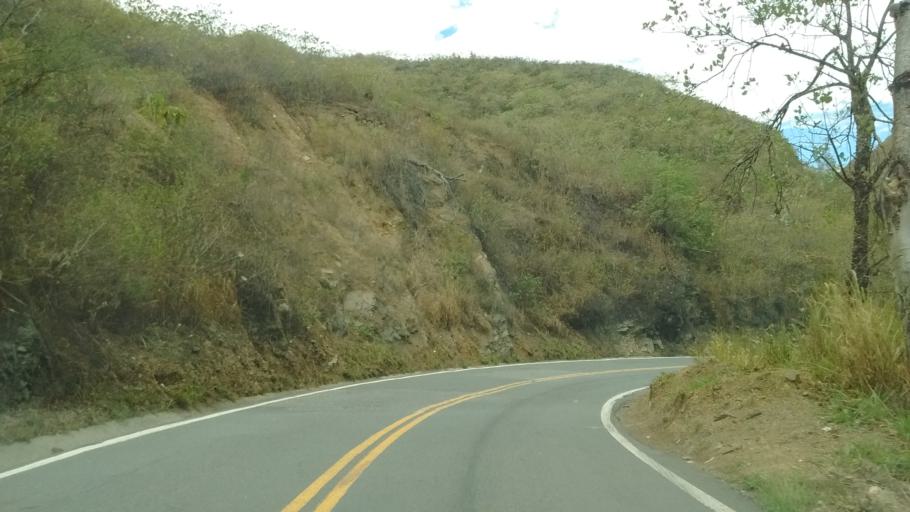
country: CO
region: Cauca
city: La Sierra
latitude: 2.2049
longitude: -76.8125
